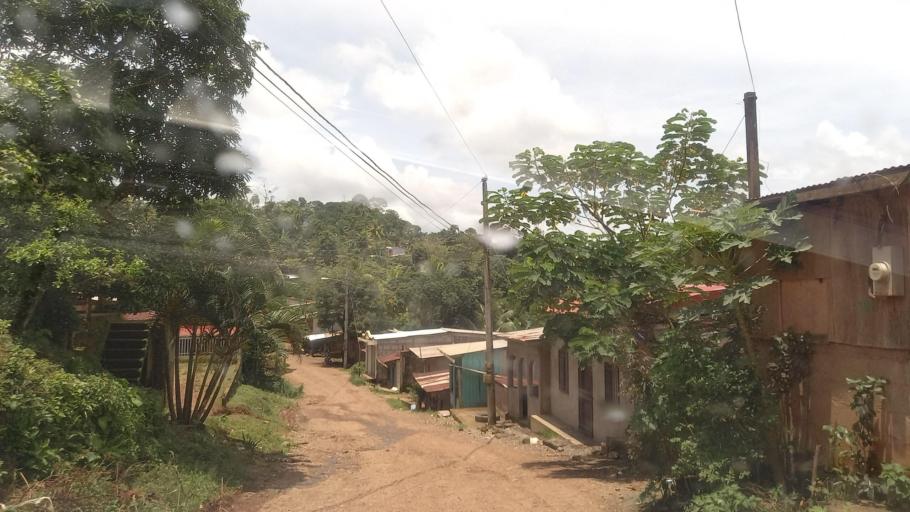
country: NI
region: Atlantico Norte (RAAN)
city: Waslala
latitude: 13.3378
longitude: -85.3716
